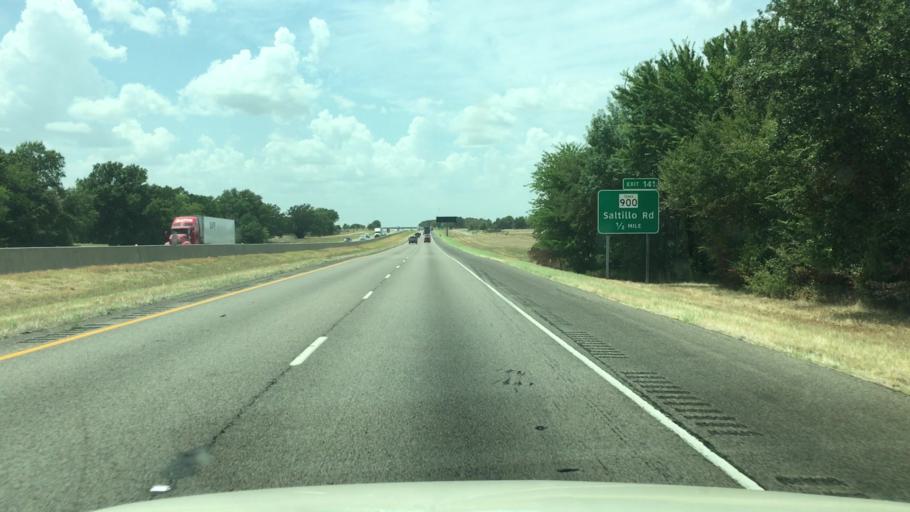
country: US
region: Texas
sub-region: Franklin County
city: Mount Vernon
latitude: 33.1669
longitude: -95.3181
